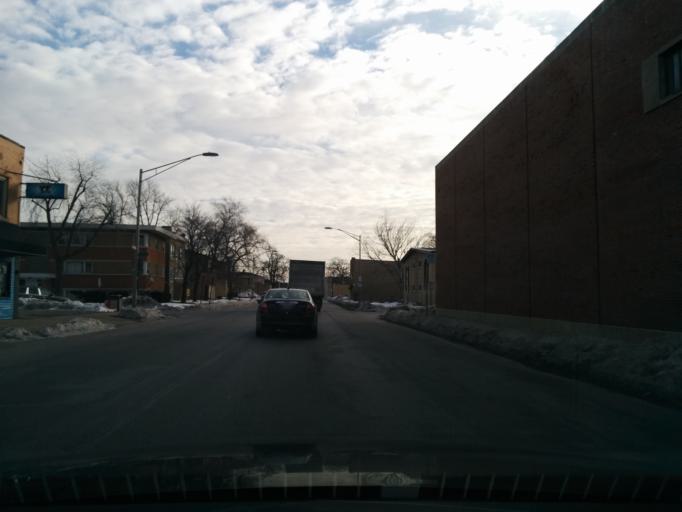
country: US
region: Illinois
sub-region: Cook County
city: Melrose Park
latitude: 41.8881
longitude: -87.8620
